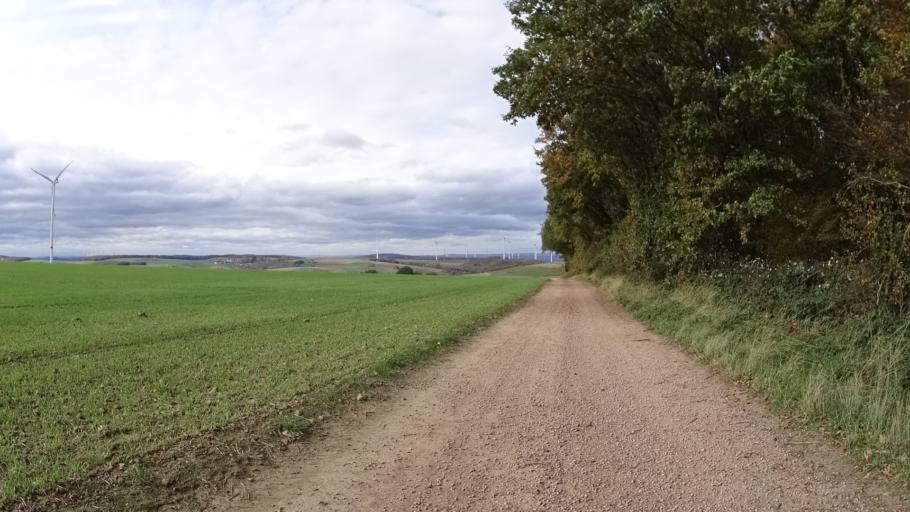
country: DE
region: Rheinland-Pfalz
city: Morsfeld
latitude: 49.7405
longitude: 7.9174
